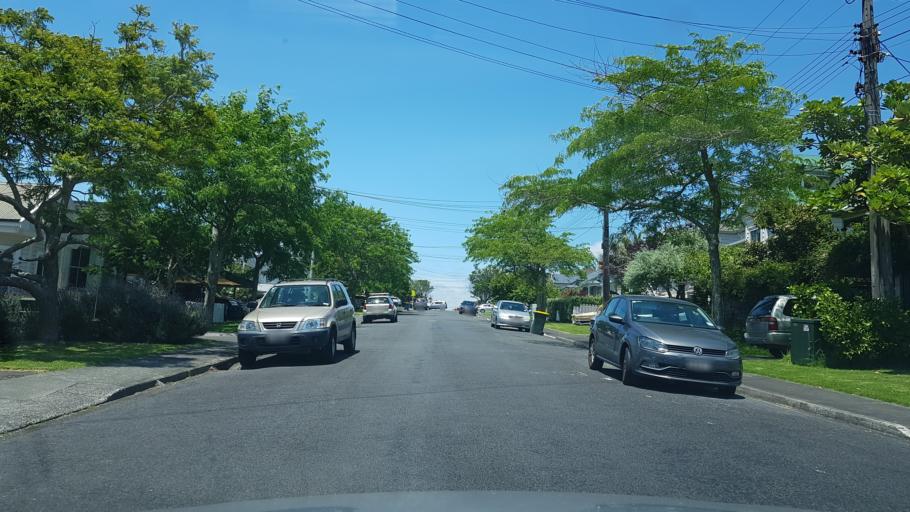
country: NZ
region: Auckland
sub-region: Auckland
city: Auckland
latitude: -36.8272
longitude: 174.7912
